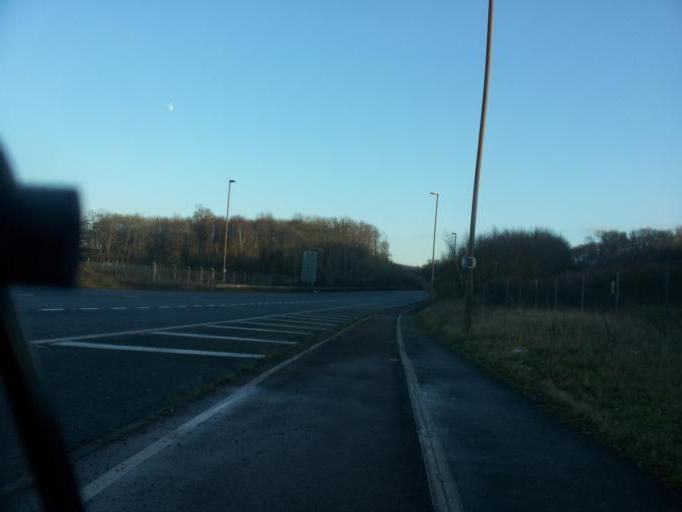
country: GB
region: England
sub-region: Medway
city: Cuxton
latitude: 51.3992
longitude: 0.4362
